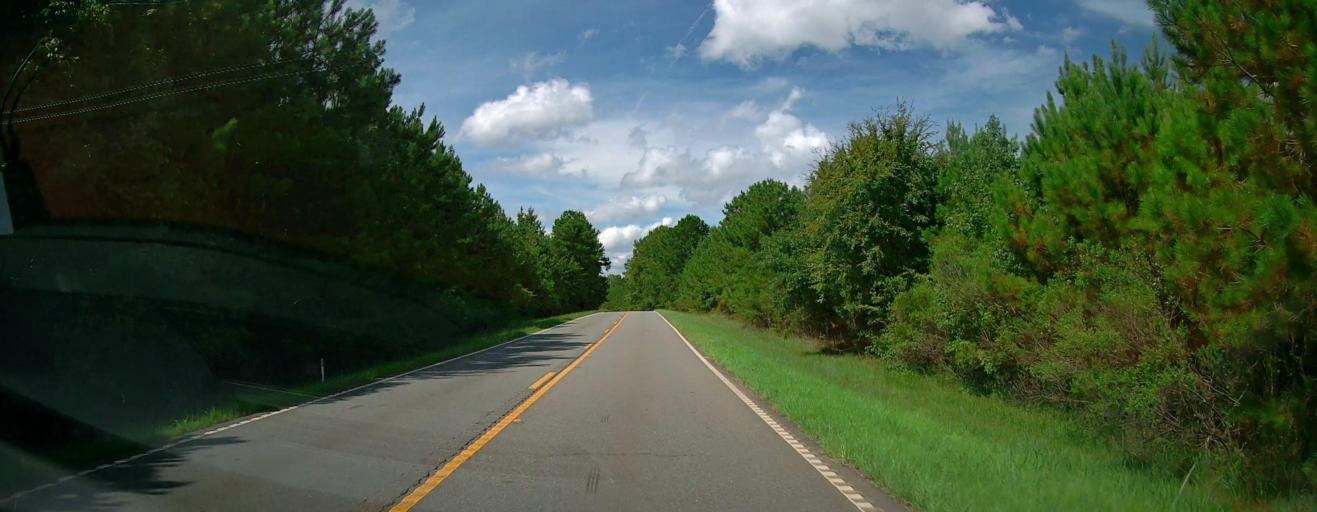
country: US
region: Georgia
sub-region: Talbot County
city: Talbotton
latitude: 32.6527
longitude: -84.5068
